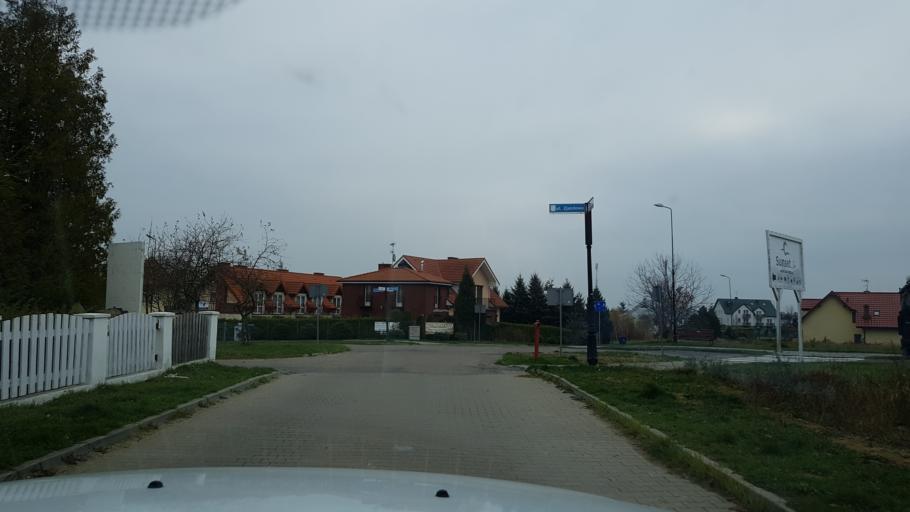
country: PL
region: West Pomeranian Voivodeship
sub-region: Powiat gryficki
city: Rewal
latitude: 54.0837
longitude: 15.0274
